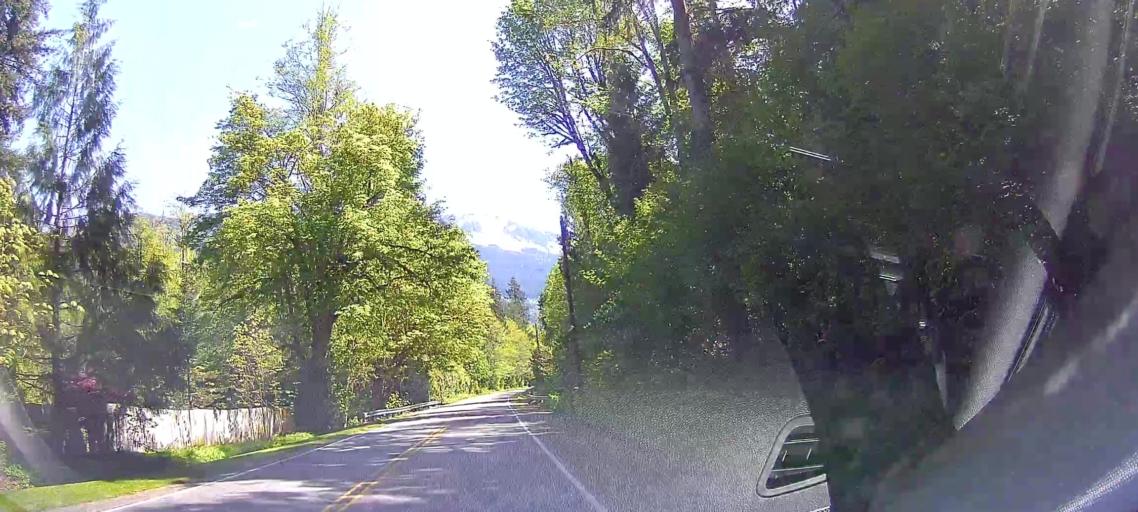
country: US
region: Washington
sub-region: Snohomish County
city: Darrington
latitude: 48.5096
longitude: -121.6819
